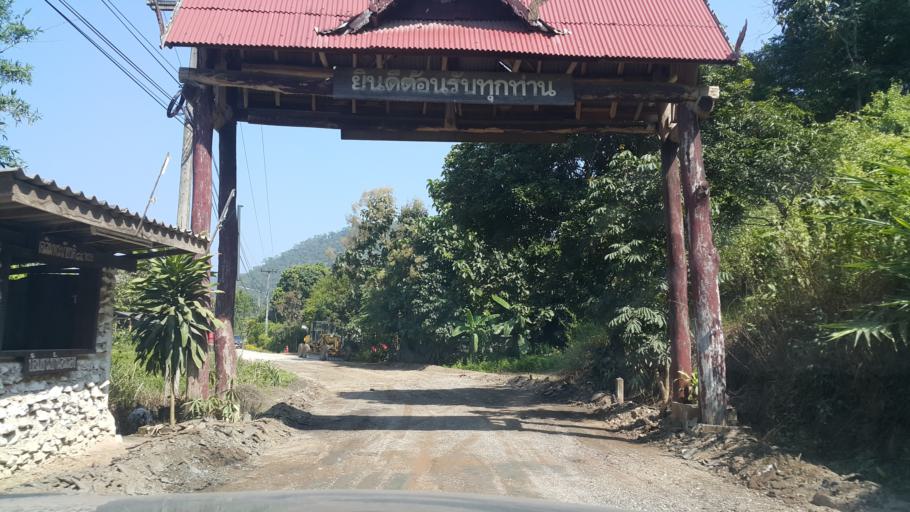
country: TH
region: Chiang Mai
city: Samoeng
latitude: 18.9069
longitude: 98.5995
